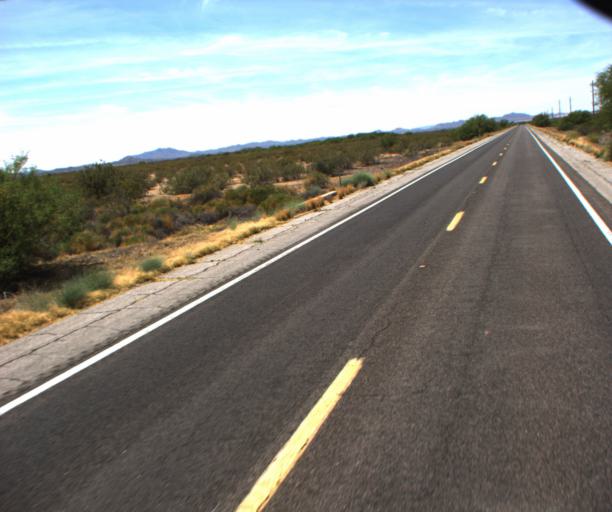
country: US
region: Arizona
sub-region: La Paz County
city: Salome
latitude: 33.8301
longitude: -113.5088
